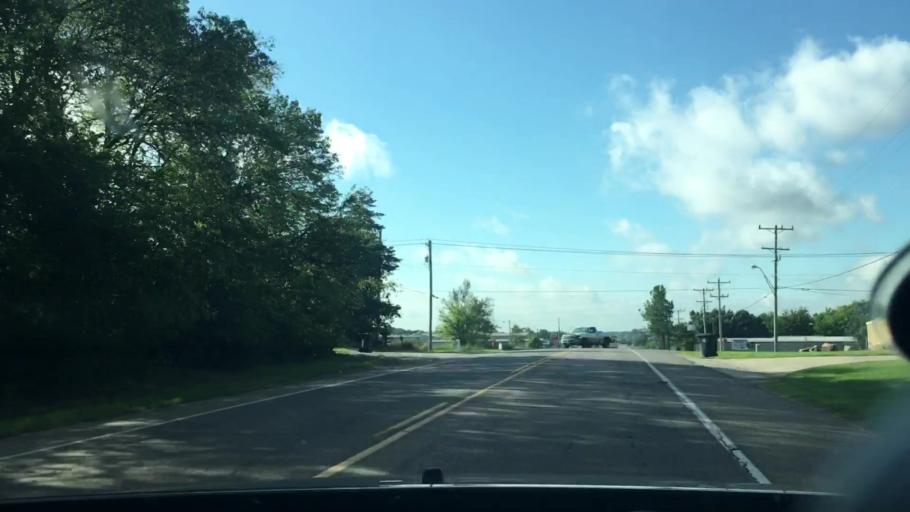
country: US
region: Oklahoma
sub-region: Bryan County
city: Durant
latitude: 34.0274
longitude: -96.3729
